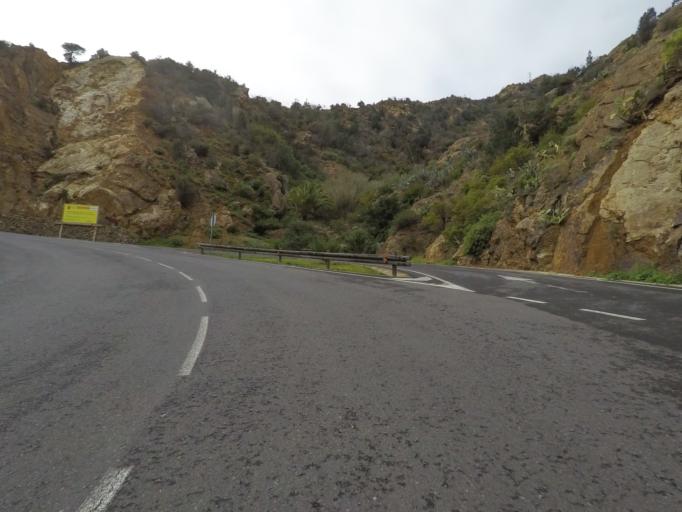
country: ES
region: Canary Islands
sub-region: Provincia de Santa Cruz de Tenerife
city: Vallehermosa
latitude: 28.1738
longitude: -17.2721
